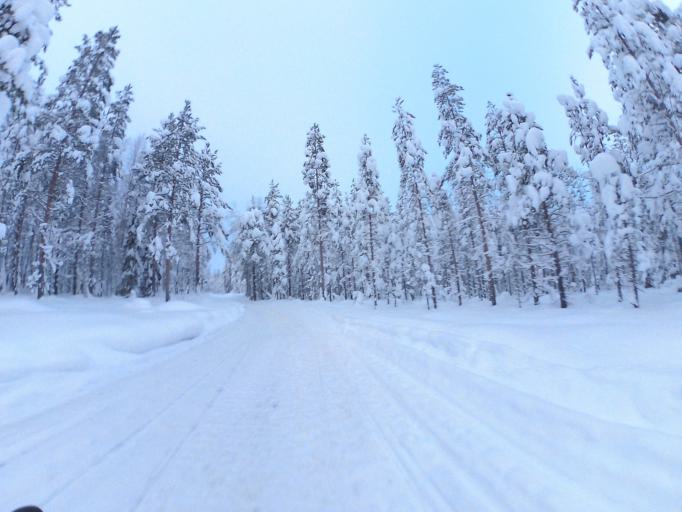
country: FI
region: Lapland
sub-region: Rovaniemi
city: Rovaniemi
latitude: 66.6311
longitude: 26.0393
